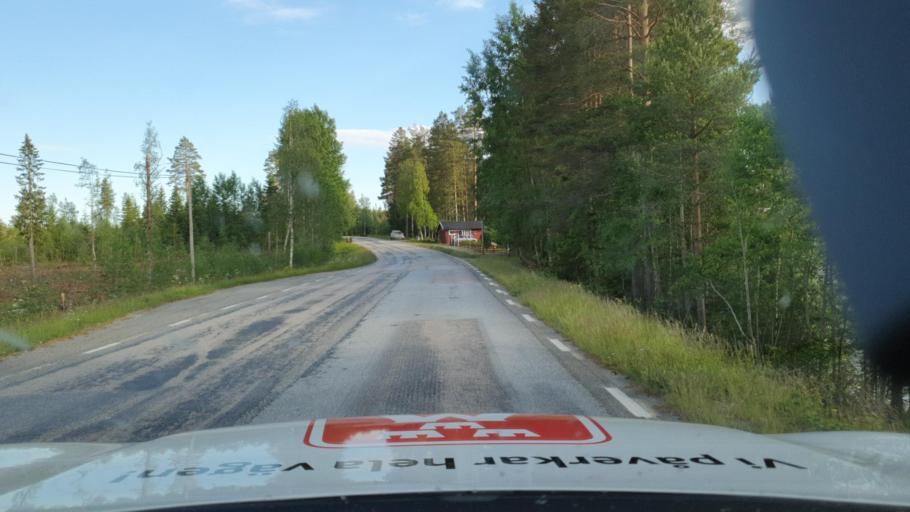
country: SE
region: Vaesterbotten
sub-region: Umea Kommun
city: Roback
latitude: 63.9066
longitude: 20.1519
